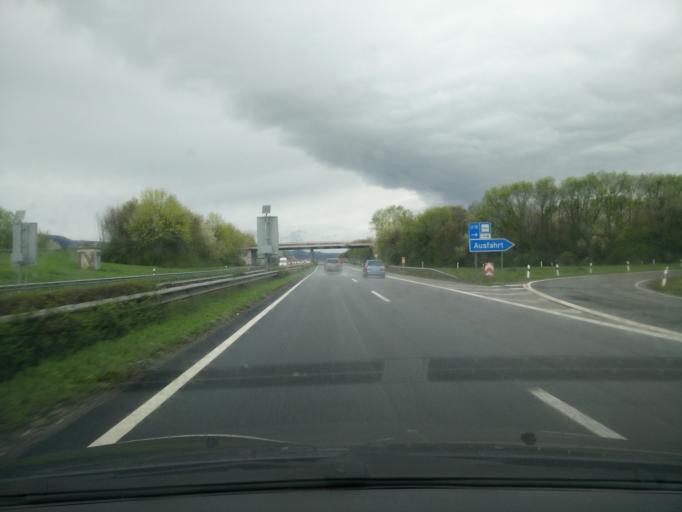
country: DE
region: Rheinland-Pfalz
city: Kirrweiler
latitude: 49.2855
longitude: 8.1529
